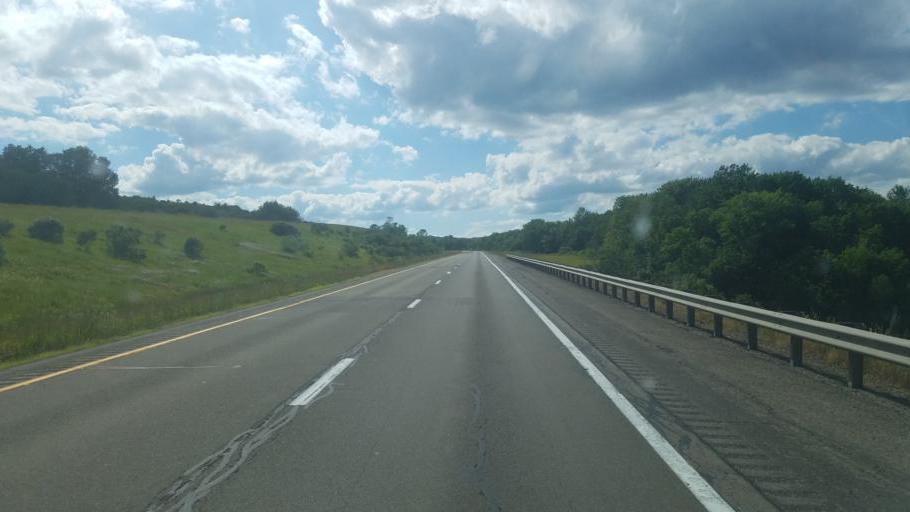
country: US
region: New York
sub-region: Allegany County
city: Alfred
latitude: 42.3186
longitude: -77.8235
